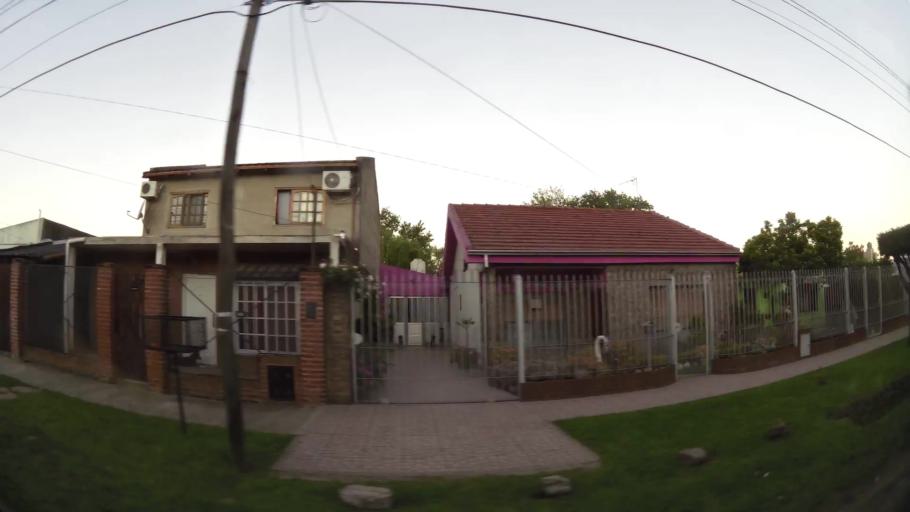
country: AR
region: Buenos Aires
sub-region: Partido de Almirante Brown
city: Adrogue
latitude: -34.7996
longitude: -58.3254
